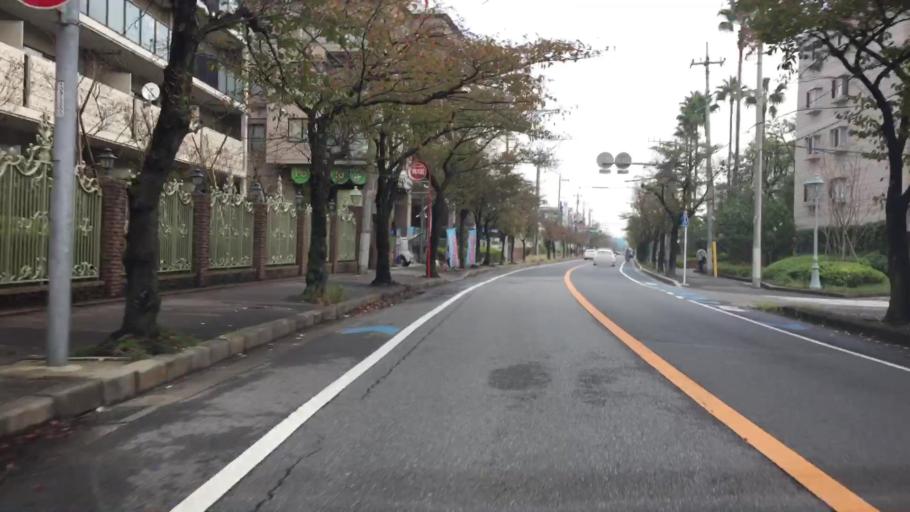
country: JP
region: Chiba
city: Kashiwa
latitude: 35.8395
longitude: 139.9674
